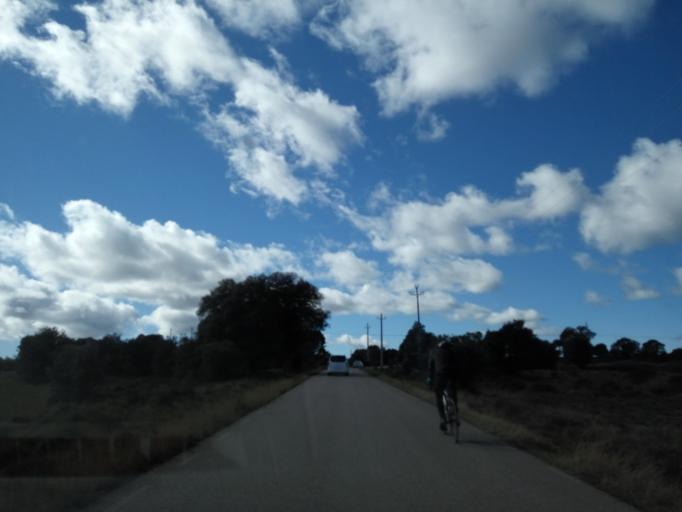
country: ES
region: Catalonia
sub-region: Provincia de Barcelona
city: Capolat
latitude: 42.0274
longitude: 1.7820
